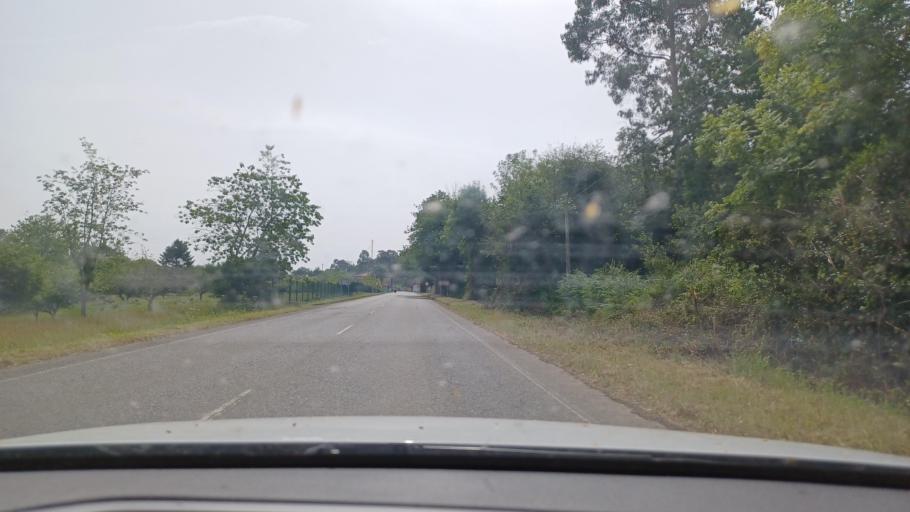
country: ES
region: Asturias
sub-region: Province of Asturias
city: Ribadesella
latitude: 43.4458
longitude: -5.0095
